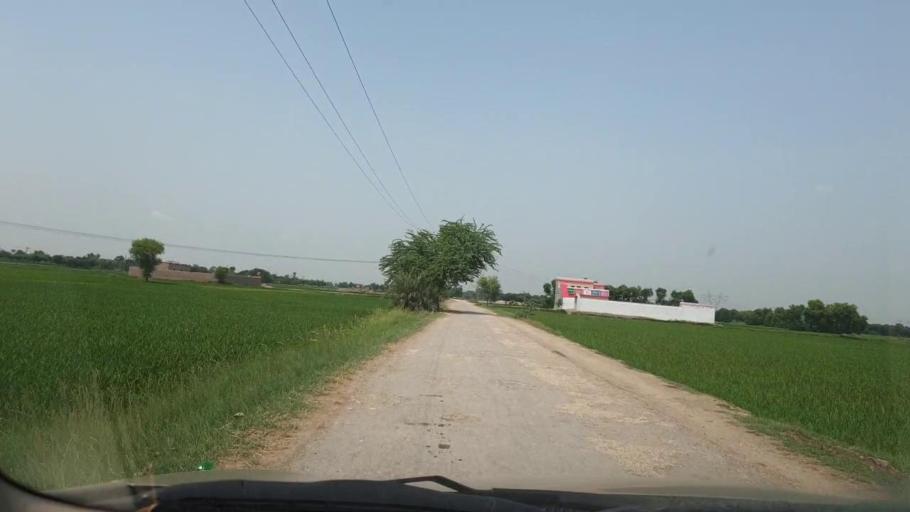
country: PK
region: Sindh
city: Larkana
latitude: 27.5773
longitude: 68.1426
